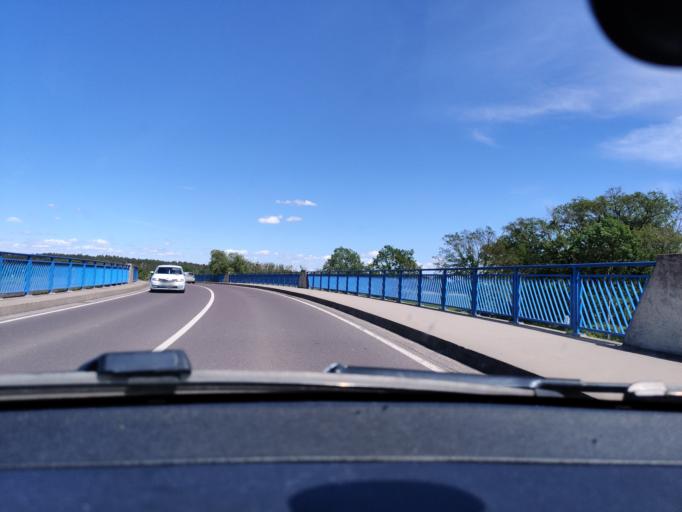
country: DE
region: Saxony-Anhalt
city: Plotzky
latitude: 52.0423
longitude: 11.7982
